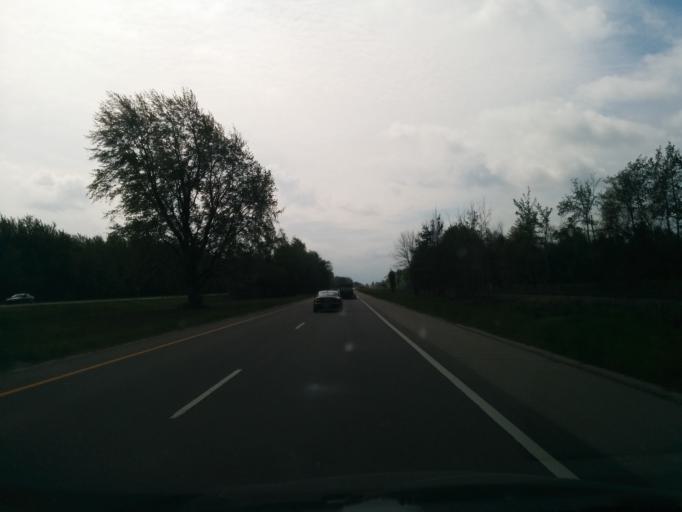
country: US
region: Michigan
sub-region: Ottawa County
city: Grand Haven
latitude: 42.9618
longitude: -86.1747
